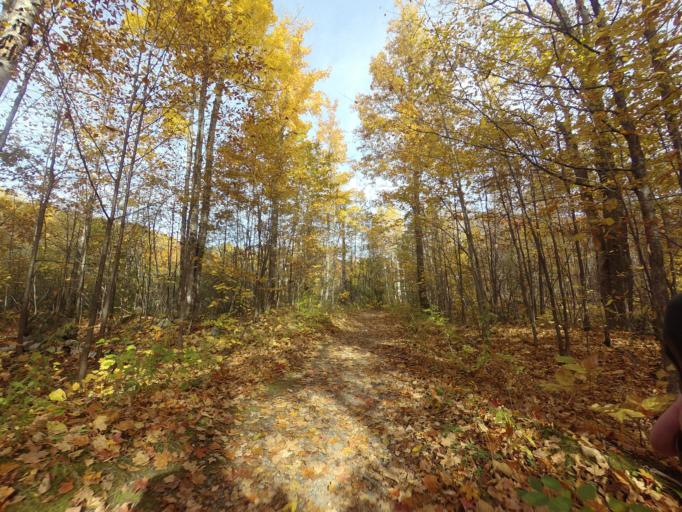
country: CA
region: Quebec
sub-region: Outaouais
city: Gatineau
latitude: 45.4702
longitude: -75.7953
